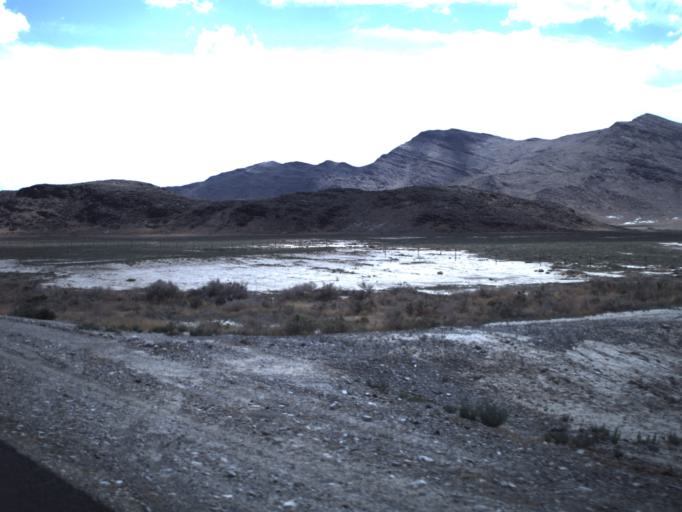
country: US
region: Utah
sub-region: Beaver County
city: Milford
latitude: 39.0600
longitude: -113.4372
